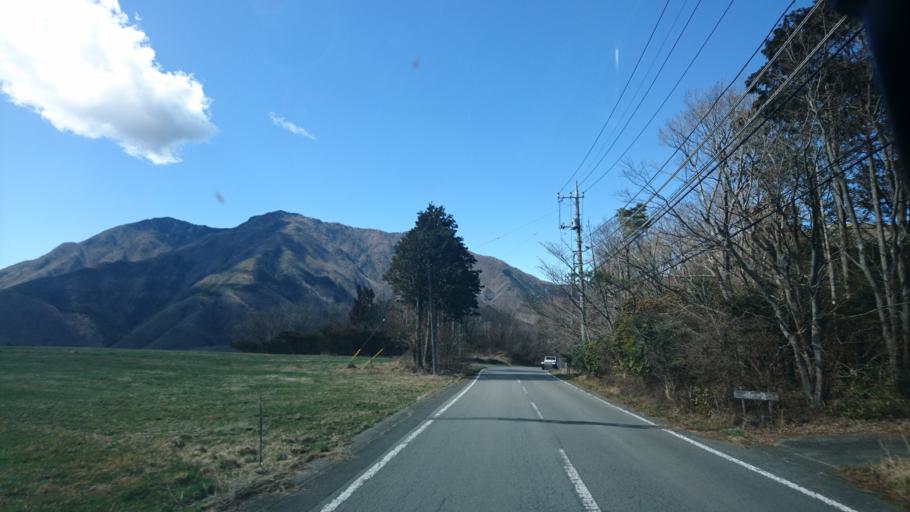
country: JP
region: Yamanashi
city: Fujikawaguchiko
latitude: 35.4234
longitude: 138.6052
